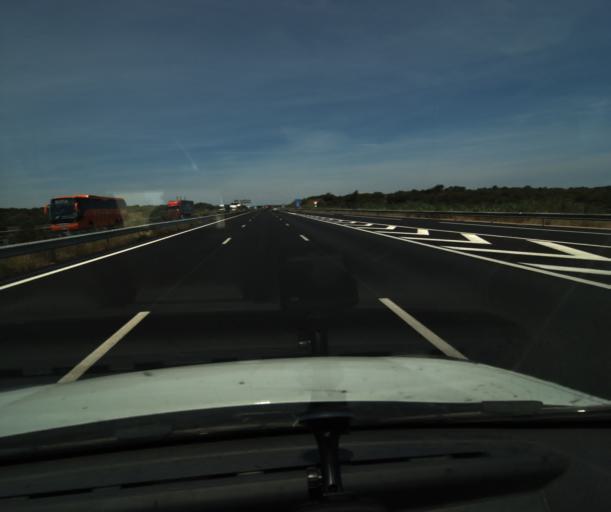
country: FR
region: Languedoc-Roussillon
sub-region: Departement de l'Aude
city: Leucate
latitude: 42.9402
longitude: 2.9702
